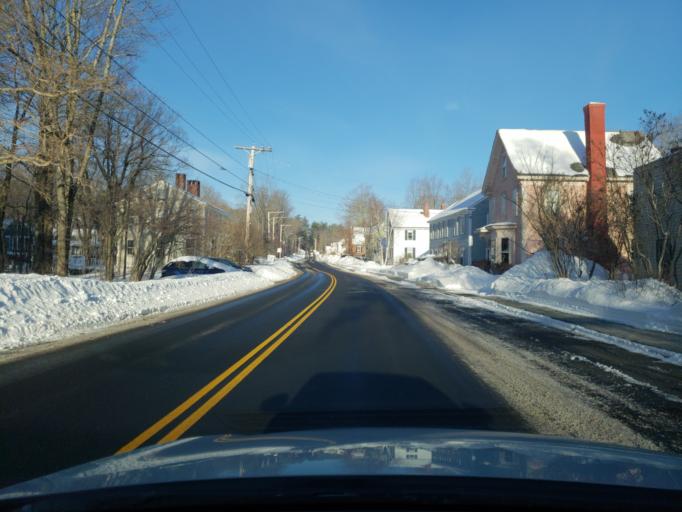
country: US
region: New Hampshire
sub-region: Hillsborough County
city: Greenfield
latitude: 42.9896
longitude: -71.8144
